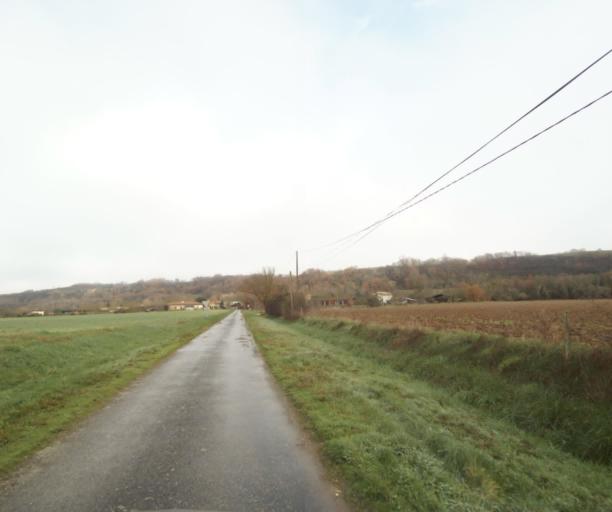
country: FR
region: Midi-Pyrenees
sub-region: Departement de la Haute-Garonne
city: Villemur-sur-Tarn
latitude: 43.8879
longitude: 1.4767
